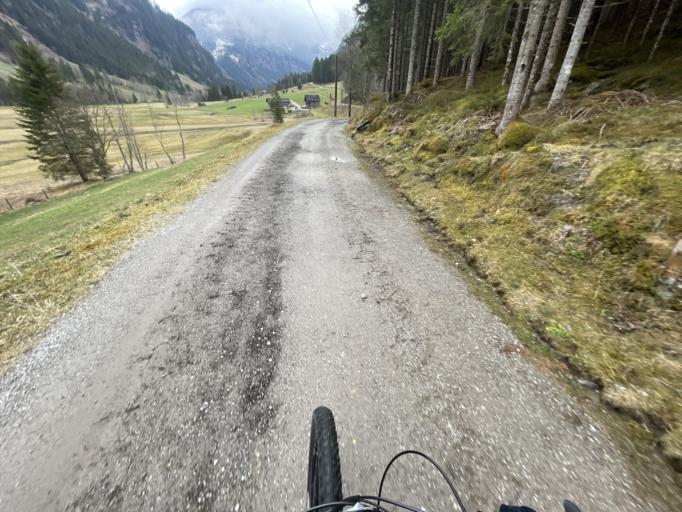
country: AT
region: Styria
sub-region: Politischer Bezirk Liezen
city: Schladming
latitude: 47.3391
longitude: 13.7367
